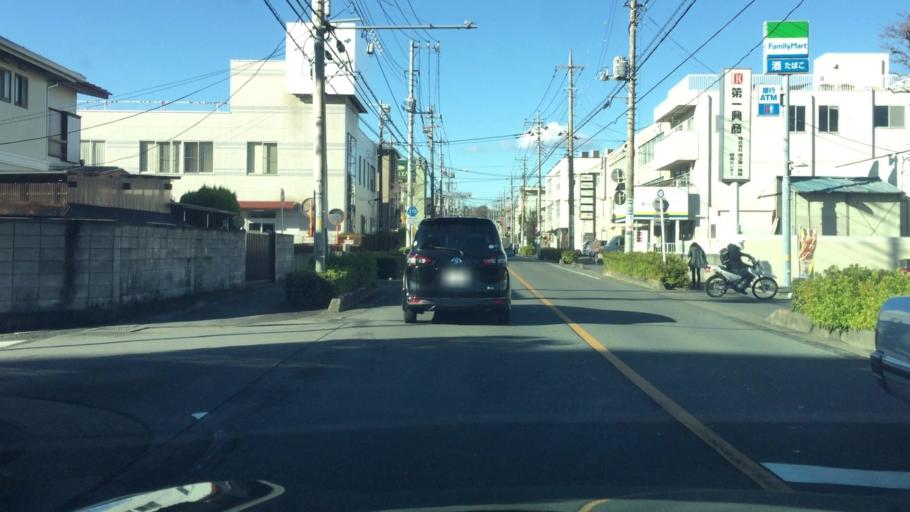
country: JP
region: Saitama
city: Yono
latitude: 35.9186
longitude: 139.6105
